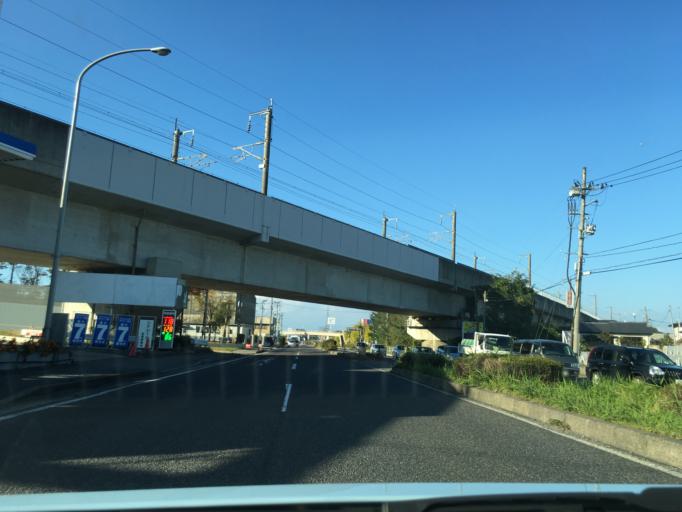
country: JP
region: Fukushima
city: Sukagawa
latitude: 37.3293
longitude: 140.3621
